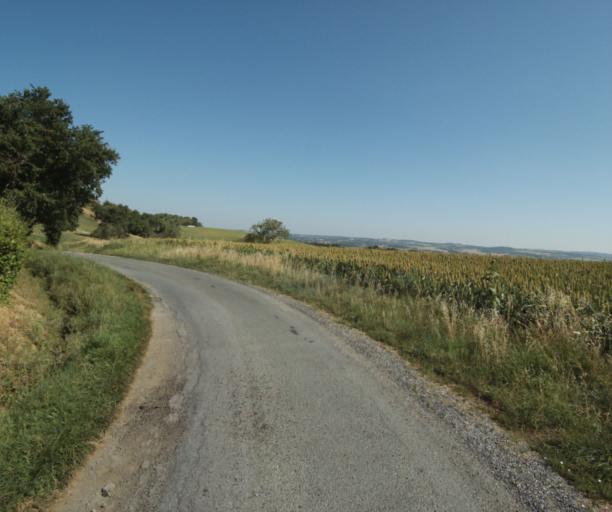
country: FR
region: Midi-Pyrenees
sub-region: Departement de la Haute-Garonne
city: Saint-Felix-Lauragais
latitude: 43.5159
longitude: 1.9355
